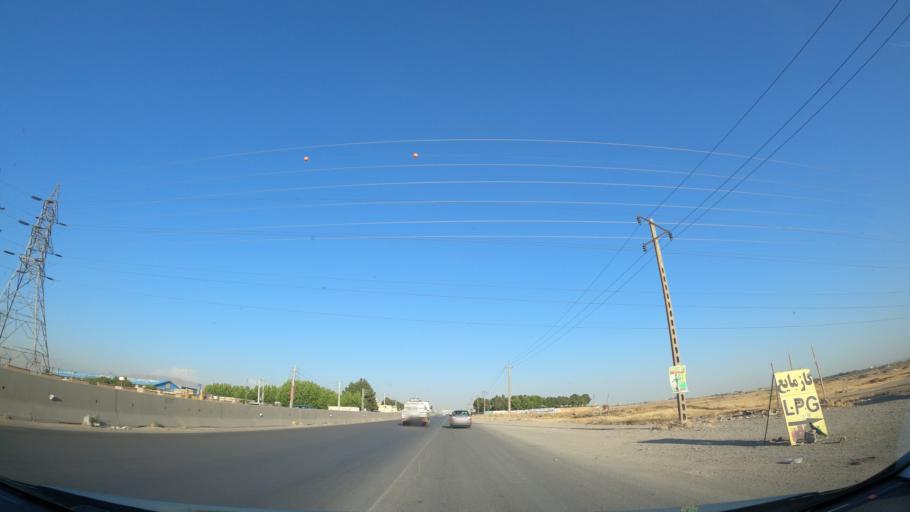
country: IR
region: Alborz
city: Hashtgerd
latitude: 35.9230
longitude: 50.7425
